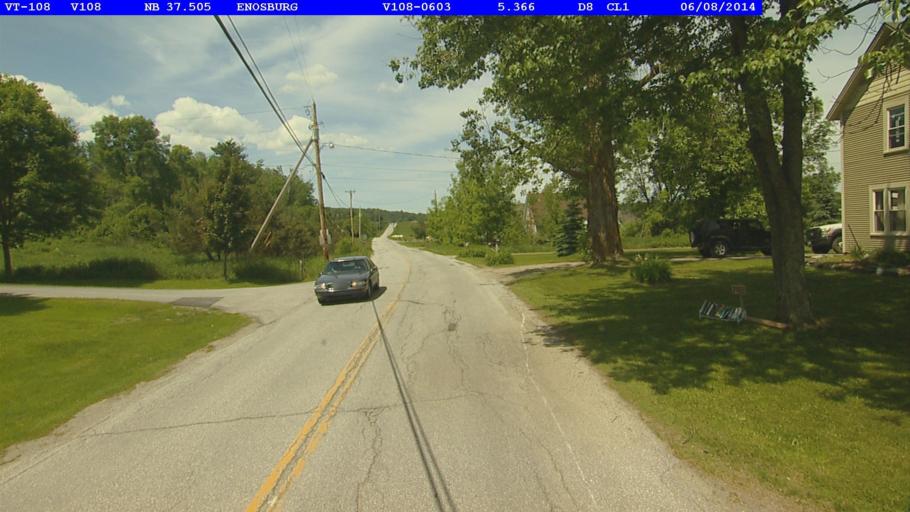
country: US
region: Vermont
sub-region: Franklin County
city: Enosburg Falls
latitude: 44.9176
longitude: -72.8059
